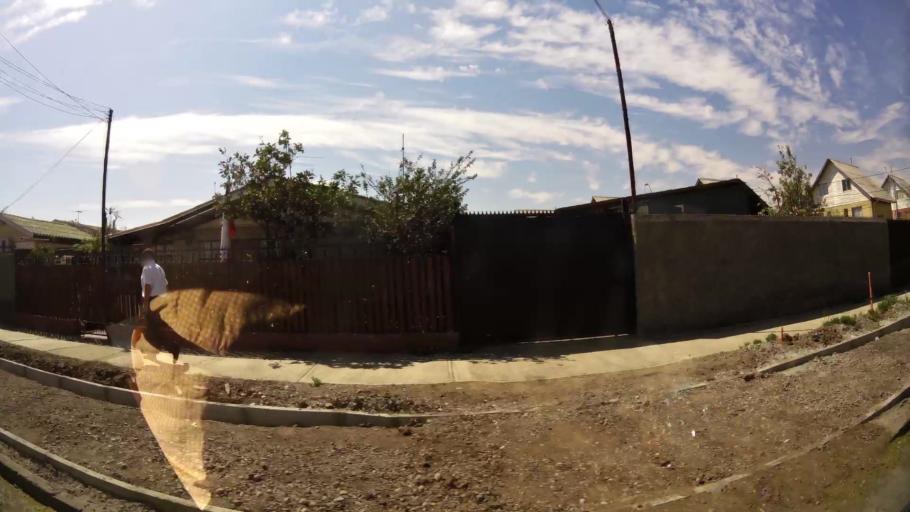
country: CL
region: Santiago Metropolitan
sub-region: Provincia de Talagante
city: Talagante
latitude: -33.6616
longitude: -70.9164
